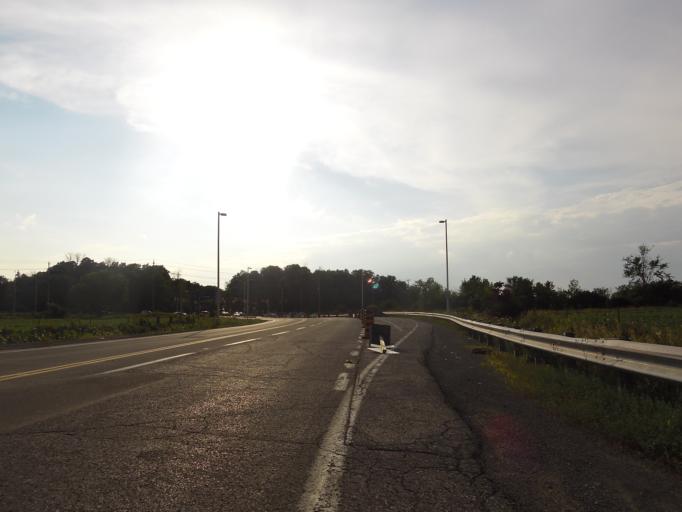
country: CA
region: Ontario
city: Bells Corners
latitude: 45.3142
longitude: -75.8801
